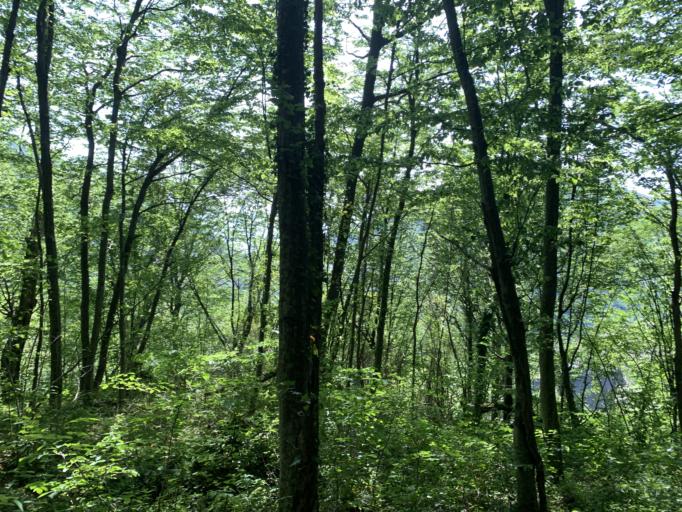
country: RU
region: Krasnodarskiy
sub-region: Sochi City
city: Lazarevskoye
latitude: 43.9506
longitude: 39.3196
